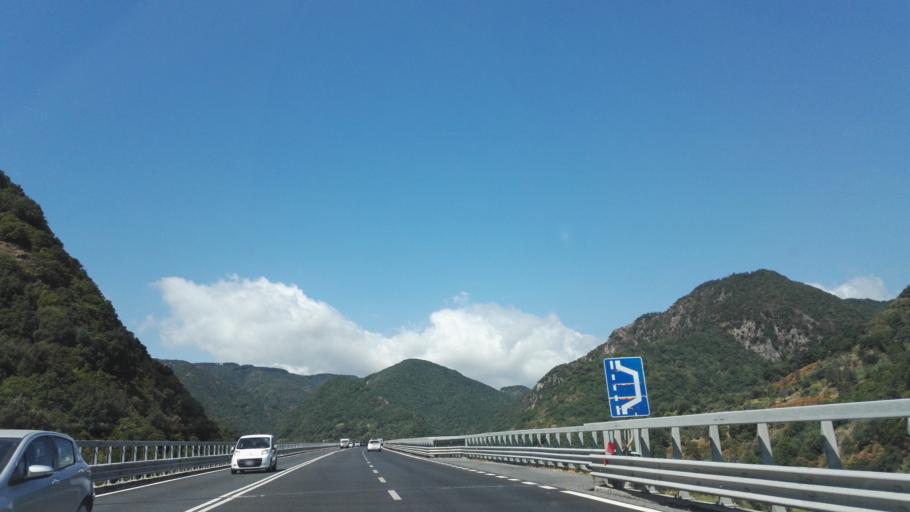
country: IT
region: Calabria
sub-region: Provincia di Reggio Calabria
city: Mammola
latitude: 38.3591
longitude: 16.2143
